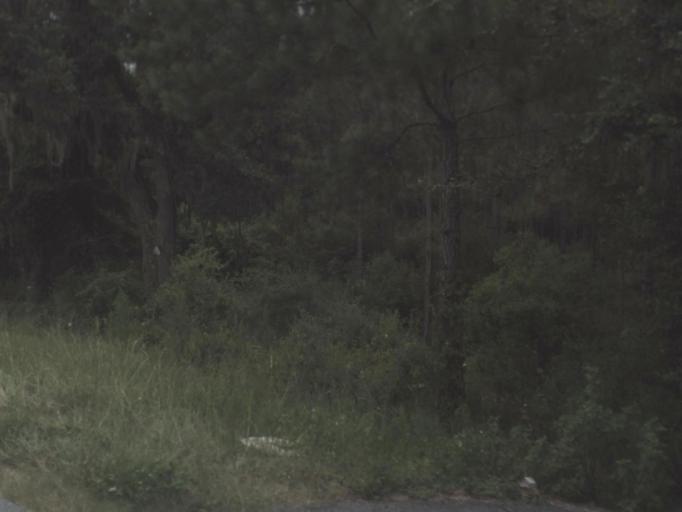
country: US
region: Florida
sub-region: Union County
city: Lake Butler
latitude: 29.9247
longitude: -82.4099
